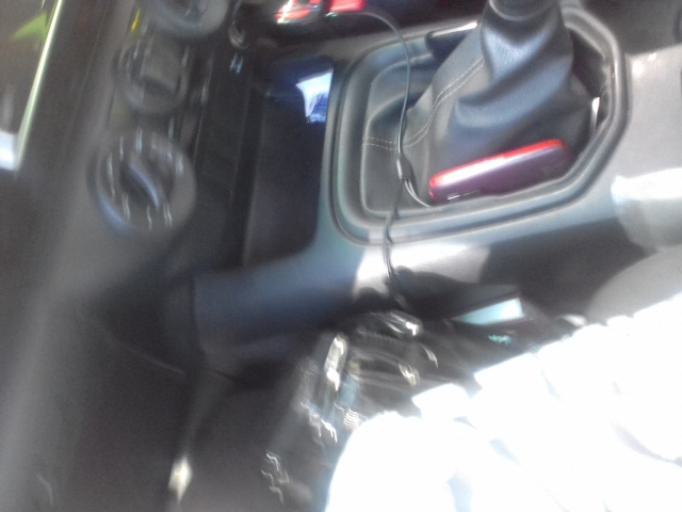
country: LS
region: Thaba-Tseka
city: Thaba-Tseka
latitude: -29.5255
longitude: 28.3462
